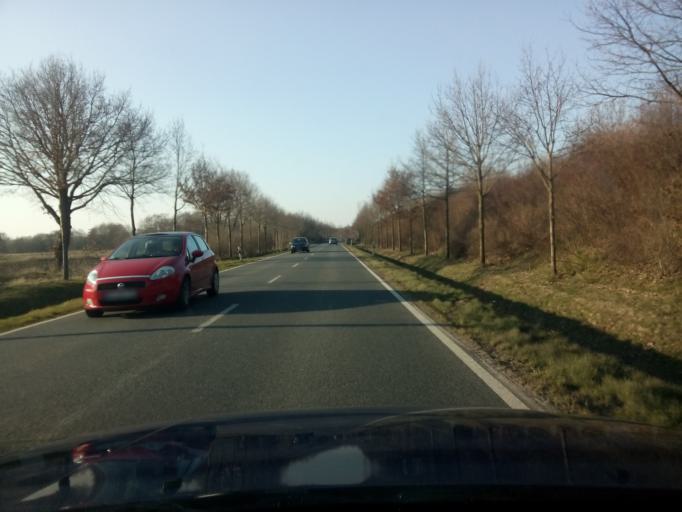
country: DE
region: Lower Saxony
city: Lilienthal
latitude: 53.1490
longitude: 8.9000
